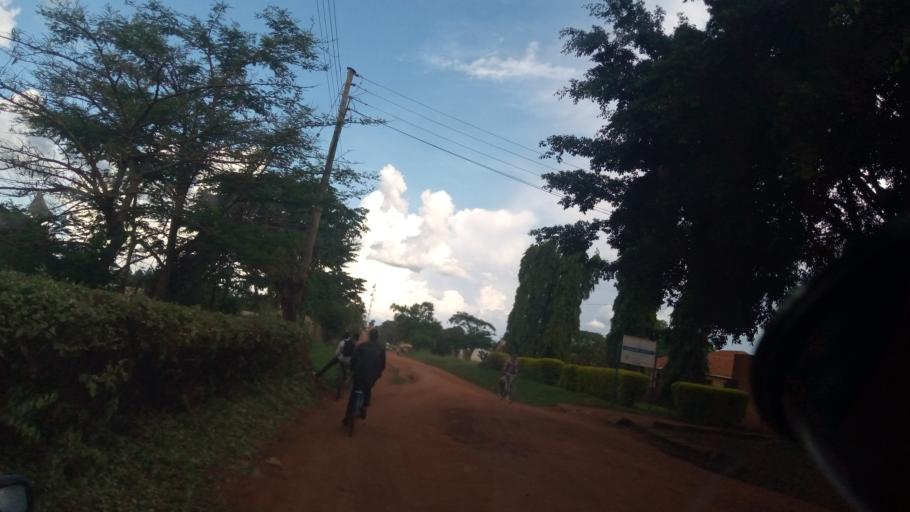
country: UG
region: Northern Region
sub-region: Lira District
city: Lira
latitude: 2.2398
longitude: 32.8980
